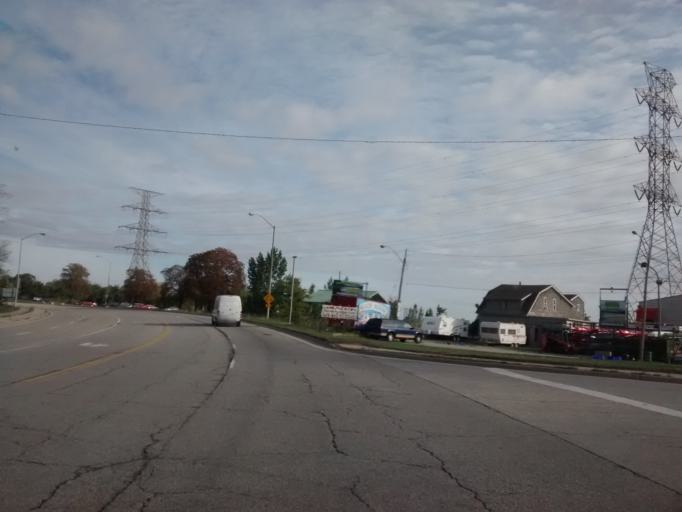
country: CA
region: Ontario
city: Hamilton
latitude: 43.2936
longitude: -79.7934
